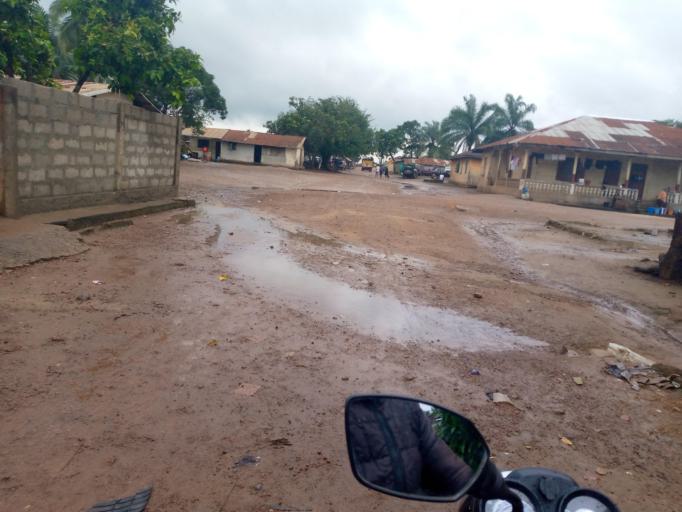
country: SL
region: Eastern Province
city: Kenema
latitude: 7.8821
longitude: -11.1845
